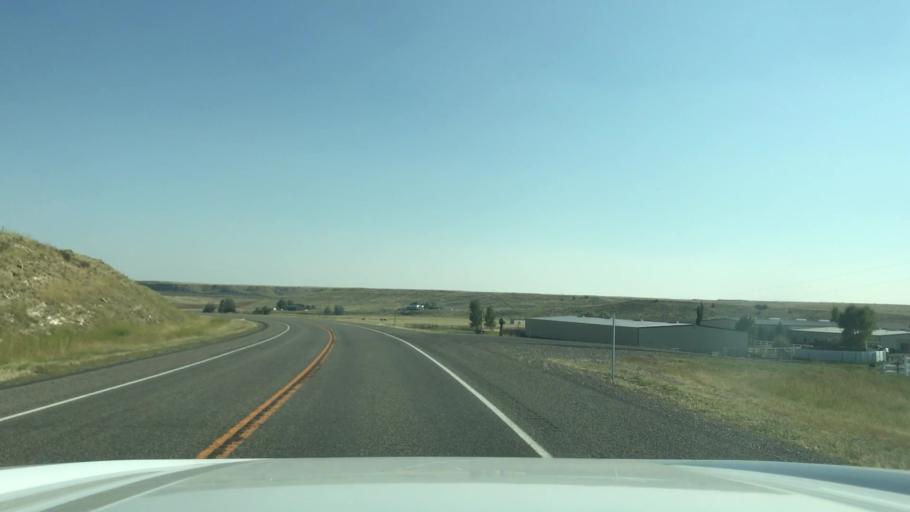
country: US
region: Montana
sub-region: Yellowstone County
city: Billings
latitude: 45.8794
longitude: -108.6699
